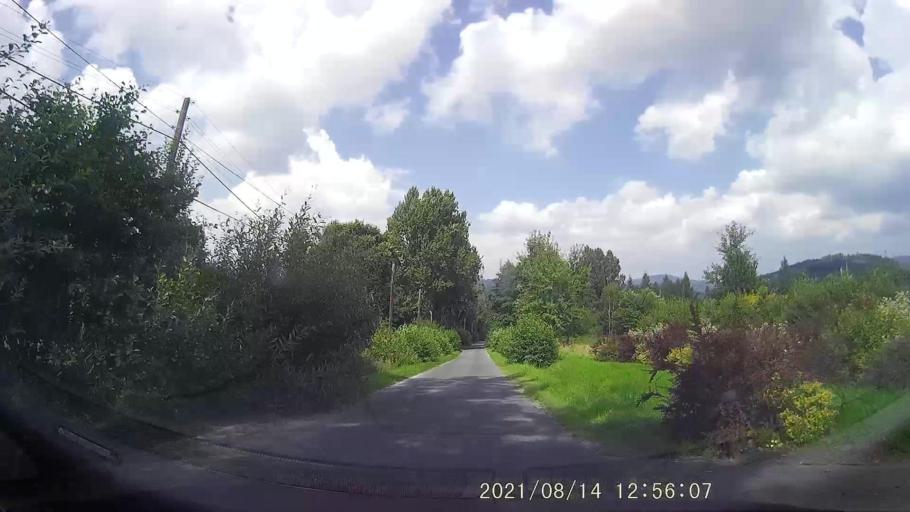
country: PL
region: Lower Silesian Voivodeship
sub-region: Powiat klodzki
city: Ladek-Zdroj
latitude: 50.3343
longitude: 16.8337
